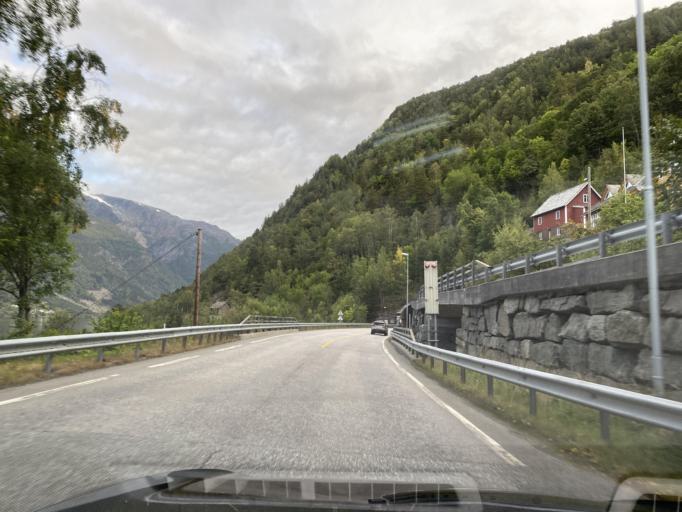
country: NO
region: Hordaland
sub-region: Odda
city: Odda
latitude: 60.1629
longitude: 6.5764
